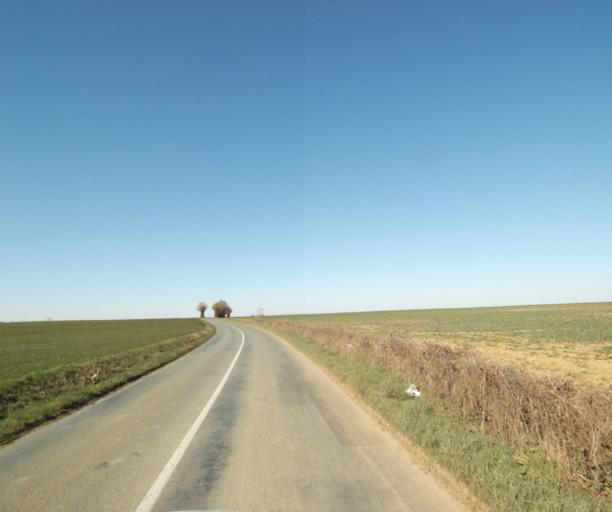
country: FR
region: Poitou-Charentes
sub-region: Departement des Deux-Sevres
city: Saint-Maxire
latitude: 46.3640
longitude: -0.4890
